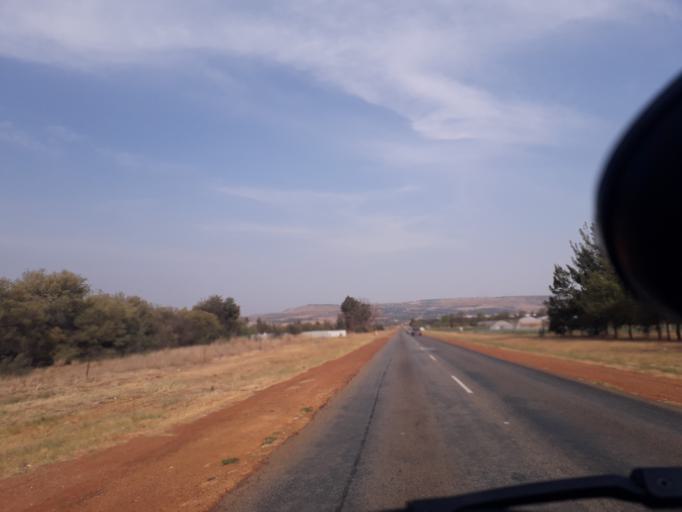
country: ZA
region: Gauteng
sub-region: West Rand District Municipality
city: Krugersdorp
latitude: -26.0035
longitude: 27.7048
